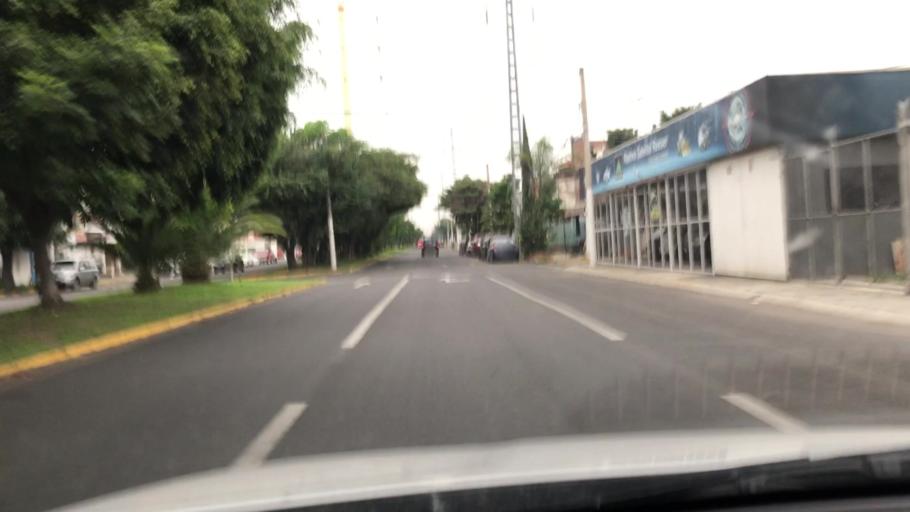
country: MX
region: Jalisco
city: Guadalajara
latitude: 20.6429
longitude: -103.4294
